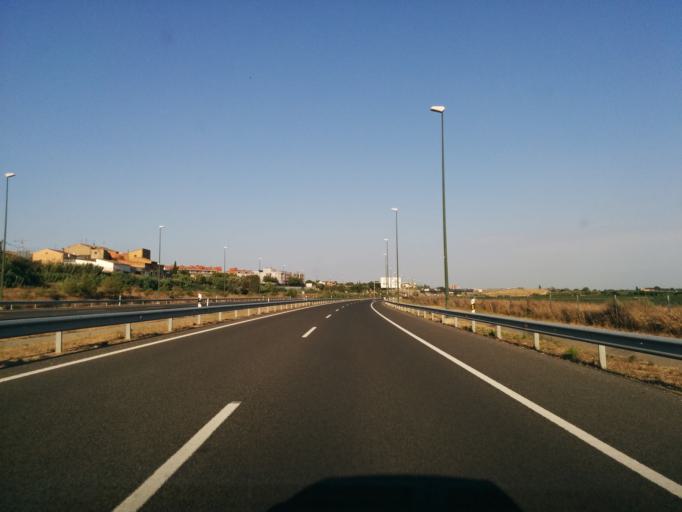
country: ES
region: Aragon
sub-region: Provincia de Zaragoza
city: Zaragoza
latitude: 41.6651
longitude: -0.8305
